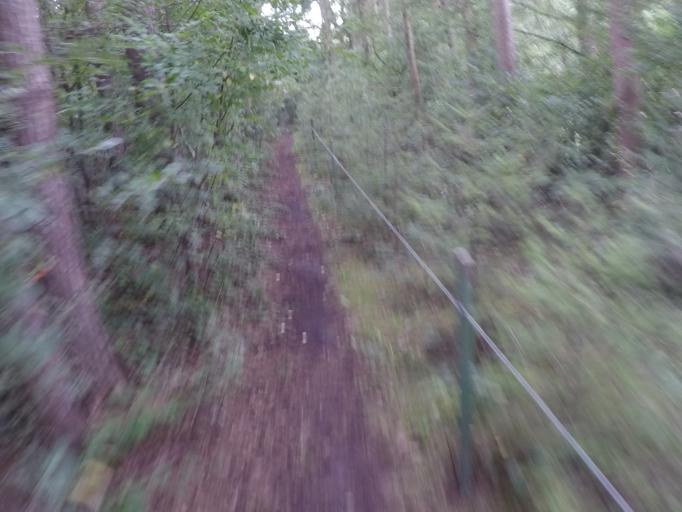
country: BE
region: Flanders
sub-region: Provincie Antwerpen
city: Grobbendonk
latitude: 51.2045
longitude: 4.7297
